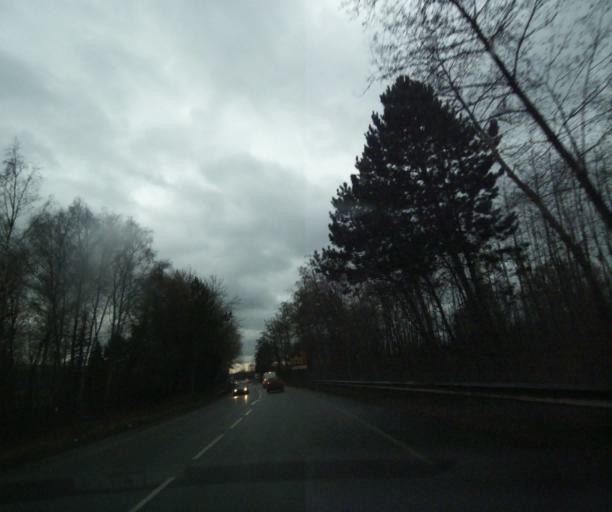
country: FR
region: Nord-Pas-de-Calais
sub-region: Departement du Nord
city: Saint-Saulve
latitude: 50.3780
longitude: 3.5415
